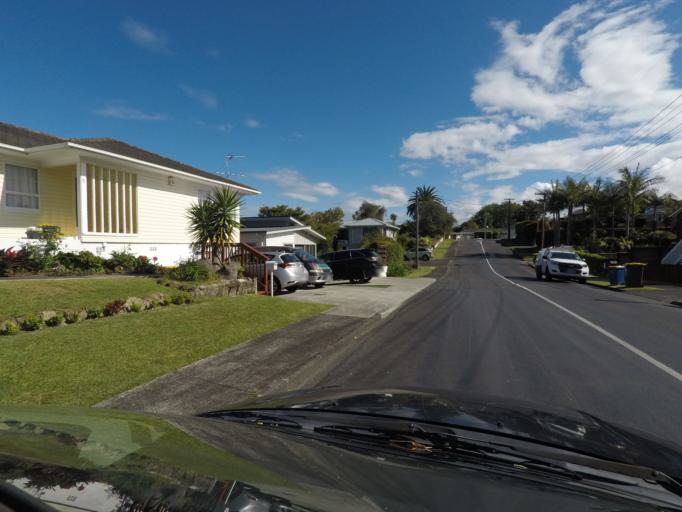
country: NZ
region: Auckland
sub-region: Auckland
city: Rosebank
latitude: -36.8604
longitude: 174.6546
